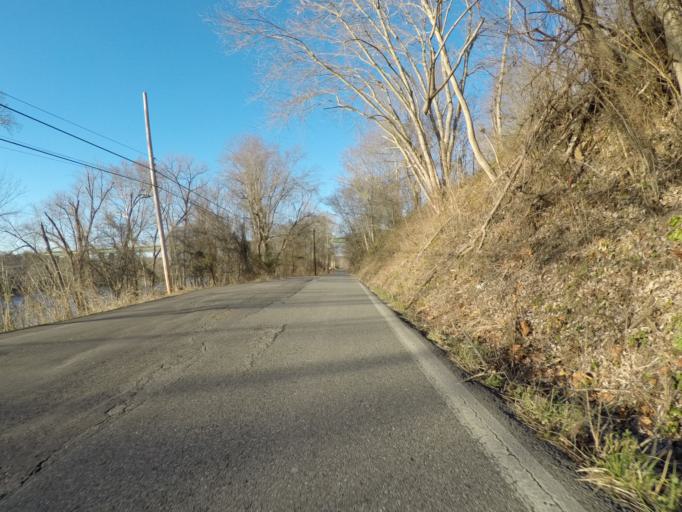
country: US
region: West Virginia
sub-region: Wayne County
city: Kenova
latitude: 38.3789
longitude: -82.5915
